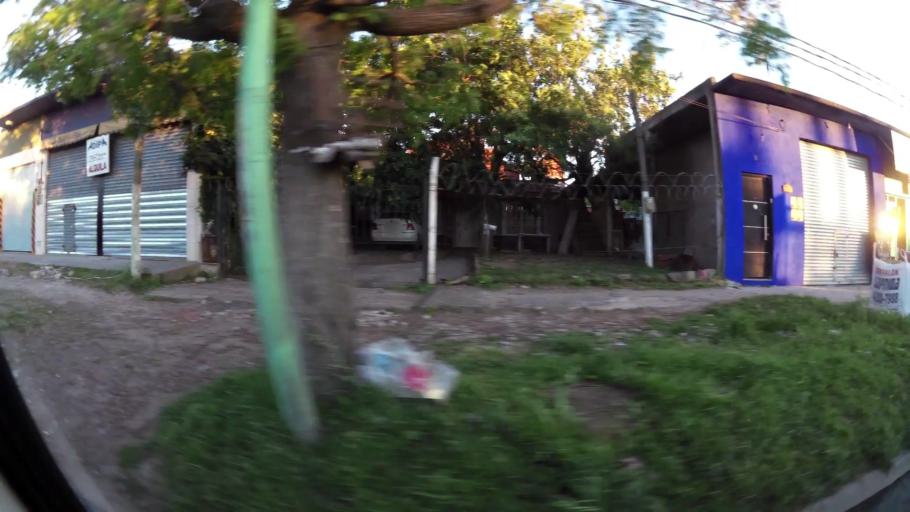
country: AR
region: Buenos Aires
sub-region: Partido de Quilmes
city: Quilmes
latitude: -34.8130
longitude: -58.1899
